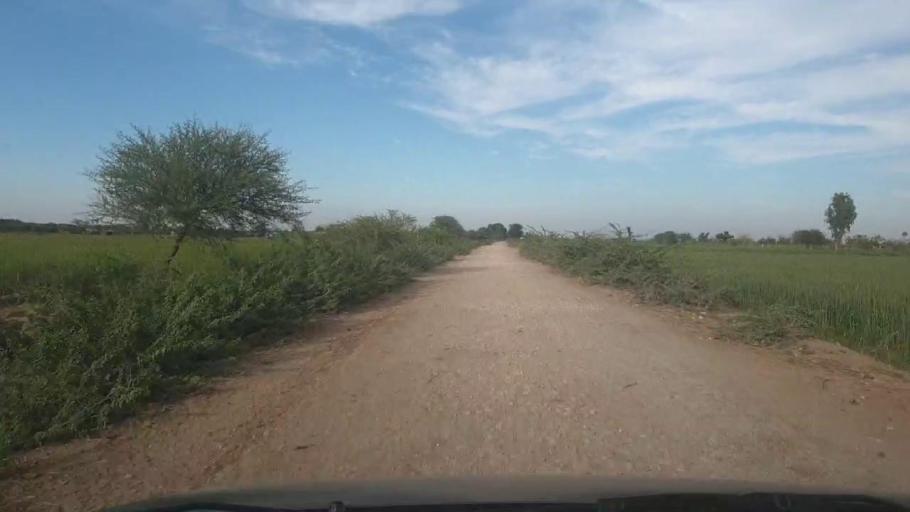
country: PK
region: Sindh
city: Samaro
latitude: 25.3268
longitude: 69.2537
